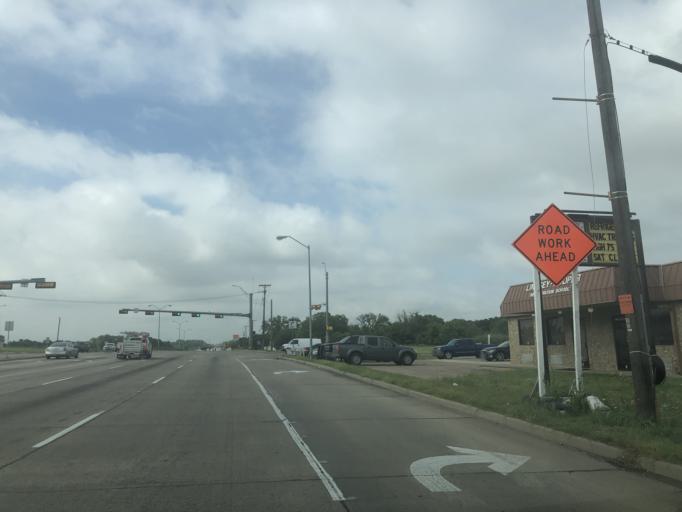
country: US
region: Texas
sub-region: Dallas County
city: Irving
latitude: 32.8059
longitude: -96.9946
